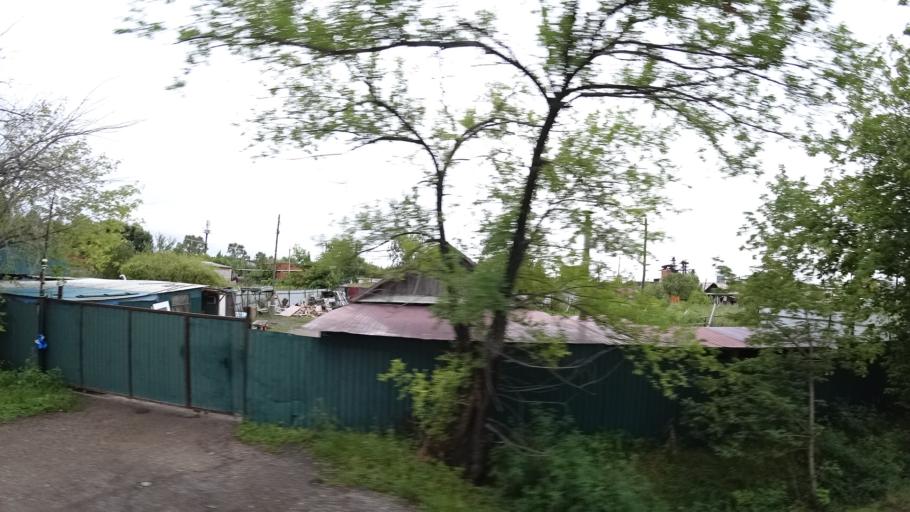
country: RU
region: Primorskiy
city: Chernigovka
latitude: 44.3349
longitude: 132.5306
